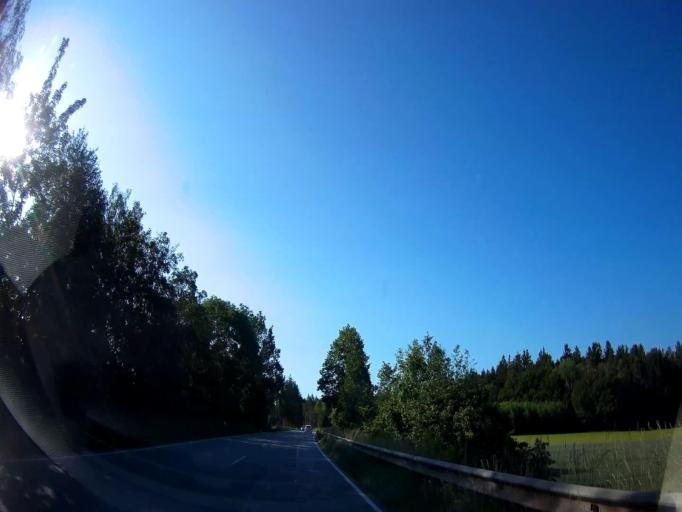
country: DE
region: Bavaria
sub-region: Lower Bavaria
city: Simbach
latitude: 48.5775
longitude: 12.7246
